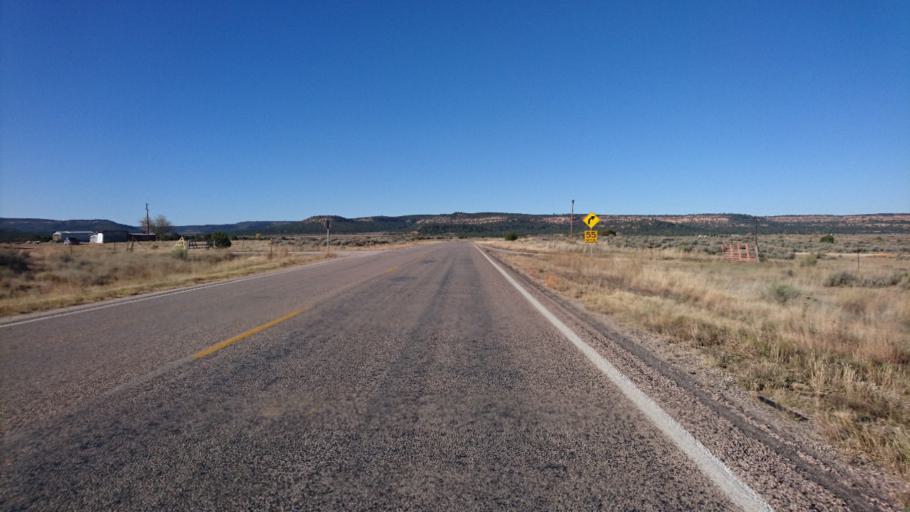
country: US
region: New Mexico
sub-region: McKinley County
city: Black Rock
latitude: 35.1073
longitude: -108.5663
